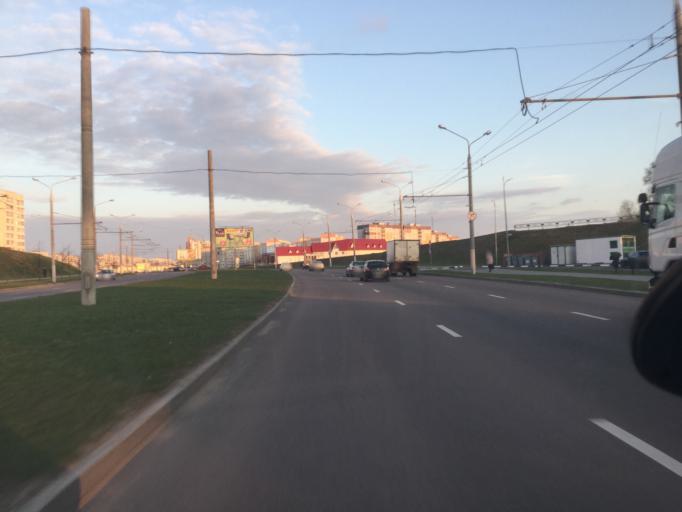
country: BY
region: Vitebsk
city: Vitebsk
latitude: 55.1667
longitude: 30.1991
